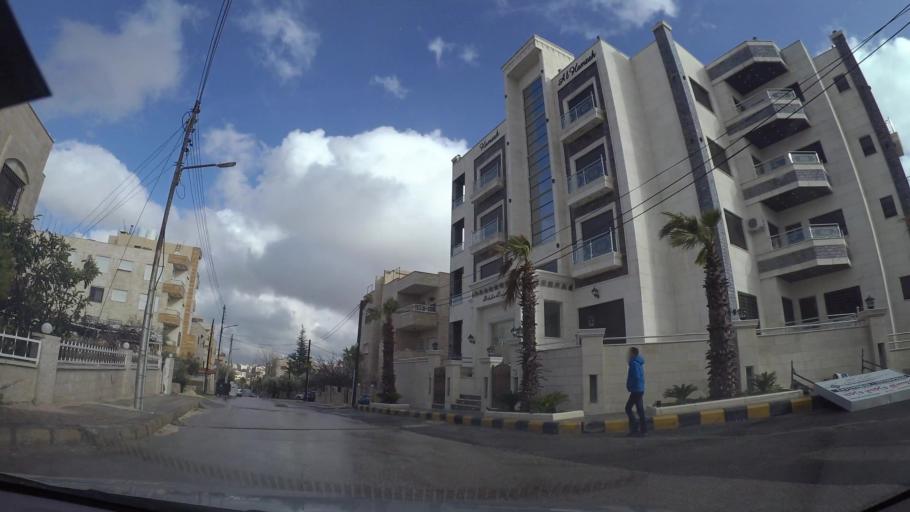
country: JO
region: Amman
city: Al Jubayhah
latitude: 32.0305
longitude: 35.8642
